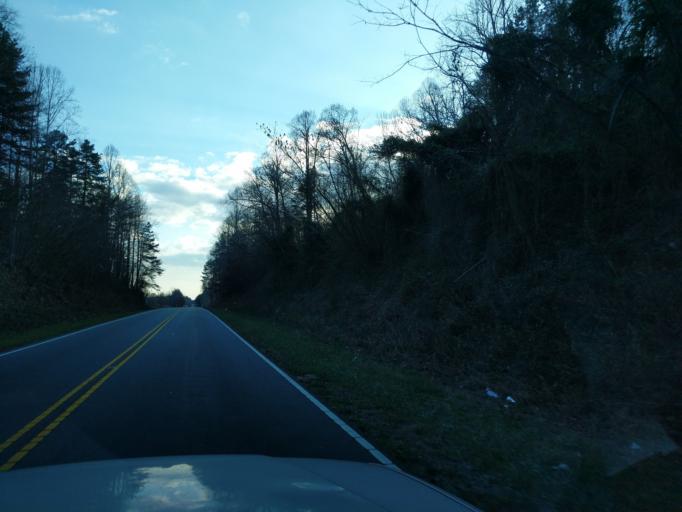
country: US
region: North Carolina
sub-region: Rutherford County
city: Rutherfordton
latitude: 35.4962
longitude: -81.9779
